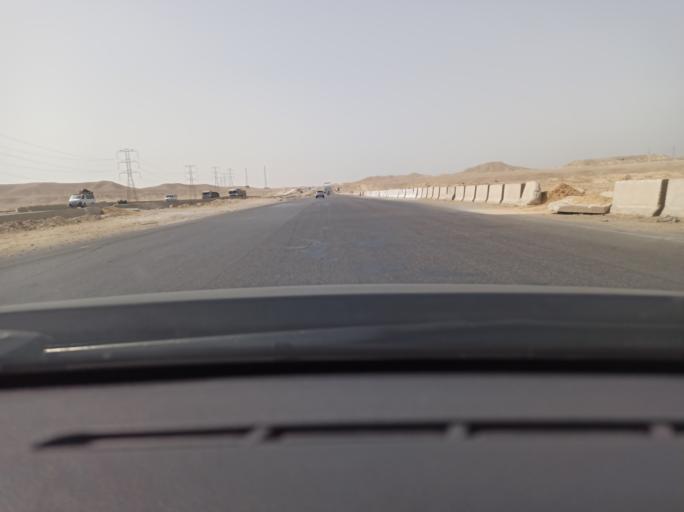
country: EG
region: Al Jizah
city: As Saff
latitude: 29.5503
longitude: 31.3960
